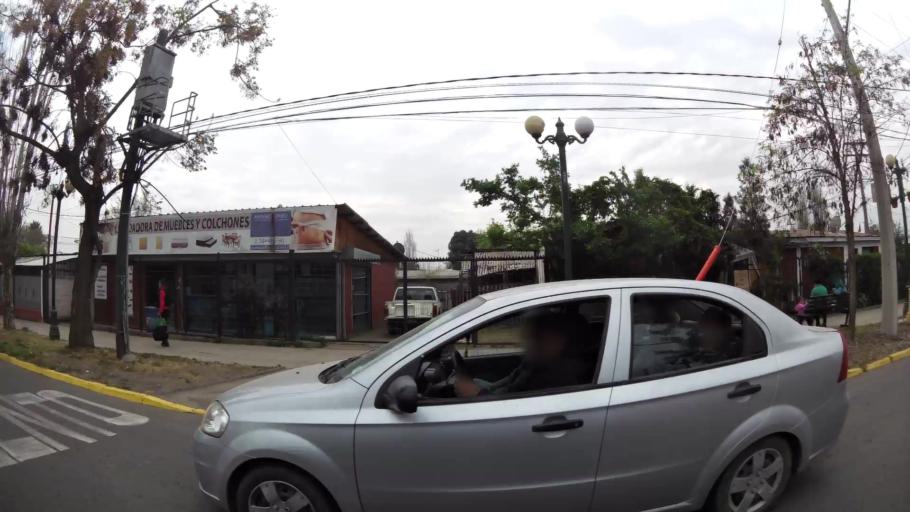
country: CL
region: Santiago Metropolitan
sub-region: Provincia de Chacabuco
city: Chicureo Abajo
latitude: -33.2047
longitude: -70.6720
